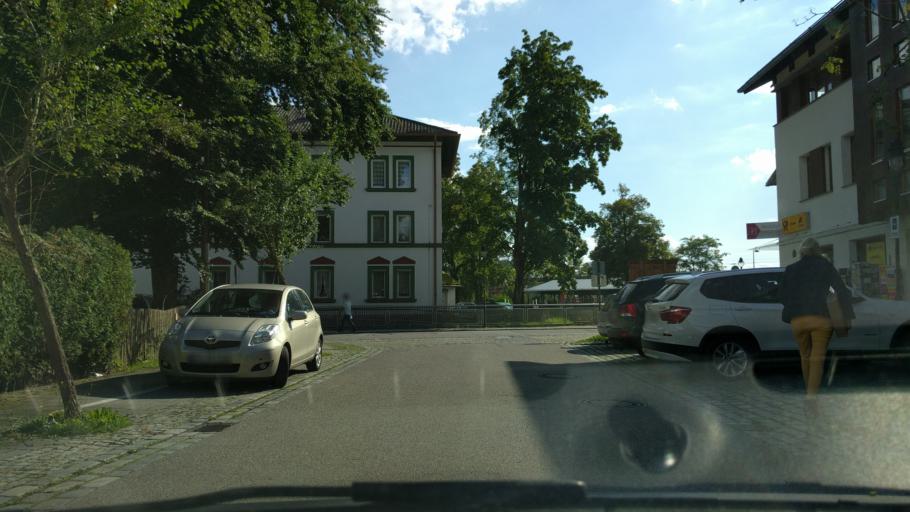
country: DE
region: Bavaria
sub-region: Upper Bavaria
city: Oberhaching
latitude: 48.0204
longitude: 11.5846
